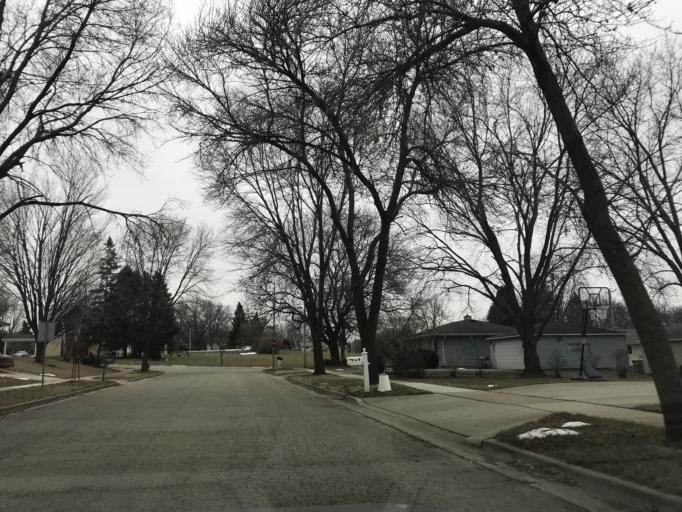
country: US
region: Wisconsin
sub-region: Dane County
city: Monona
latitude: 43.0997
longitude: -89.2971
